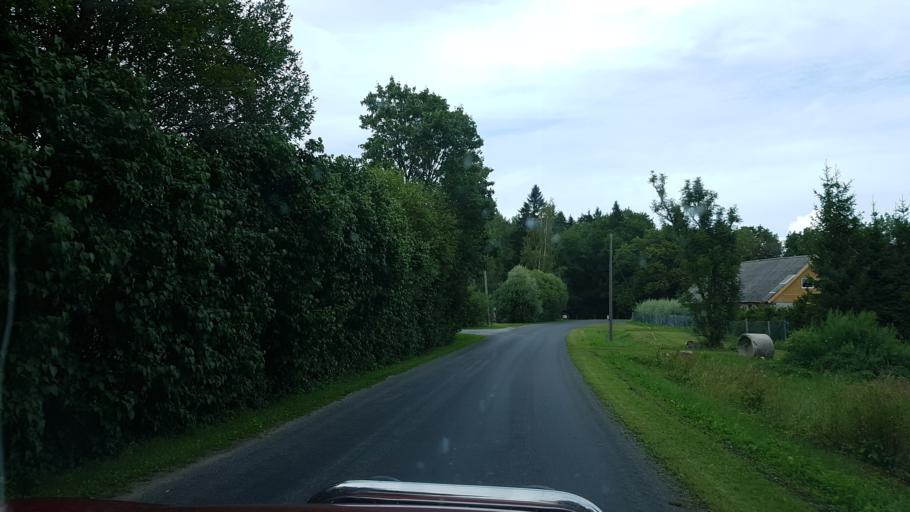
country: EE
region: Laeaene
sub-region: Ridala Parish
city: Uuemoisa
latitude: 59.0021
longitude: 23.7213
